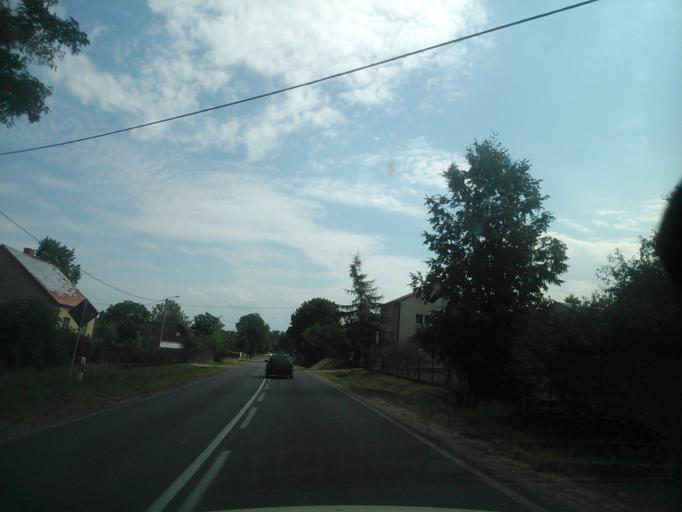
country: PL
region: Warmian-Masurian Voivodeship
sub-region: Powiat dzialdowski
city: Ilowo -Osada
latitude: 53.1541
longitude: 20.3185
